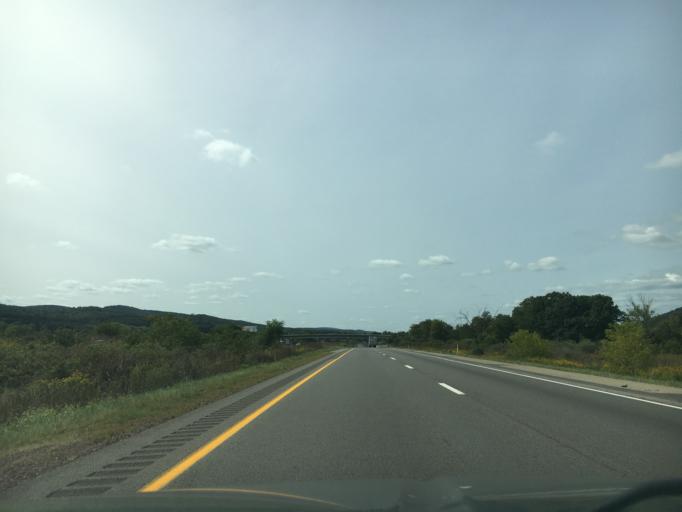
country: US
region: Pennsylvania
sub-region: Montour County
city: Mechanicsville
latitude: 41.0051
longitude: -76.5614
